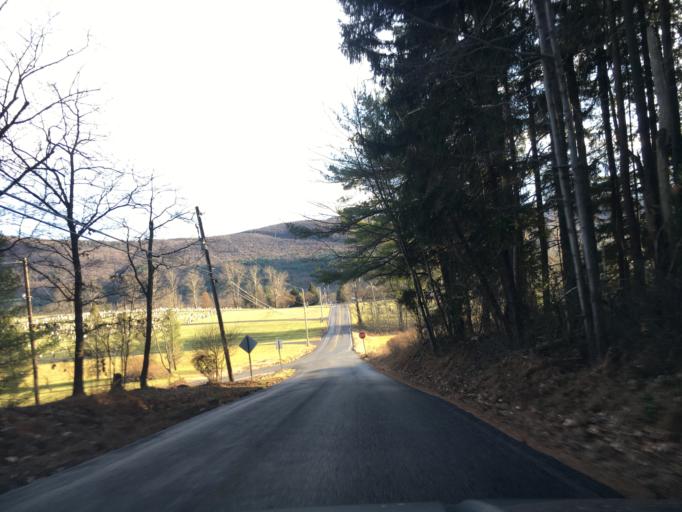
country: US
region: Pennsylvania
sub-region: Carbon County
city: Lehighton
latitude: 40.7894
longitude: -75.7160
